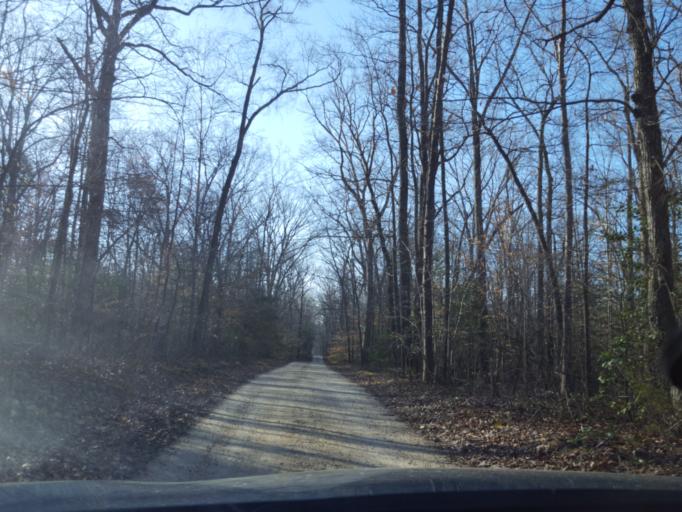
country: US
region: Maryland
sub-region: Prince George's County
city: Baden
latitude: 38.6355
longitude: -76.8128
